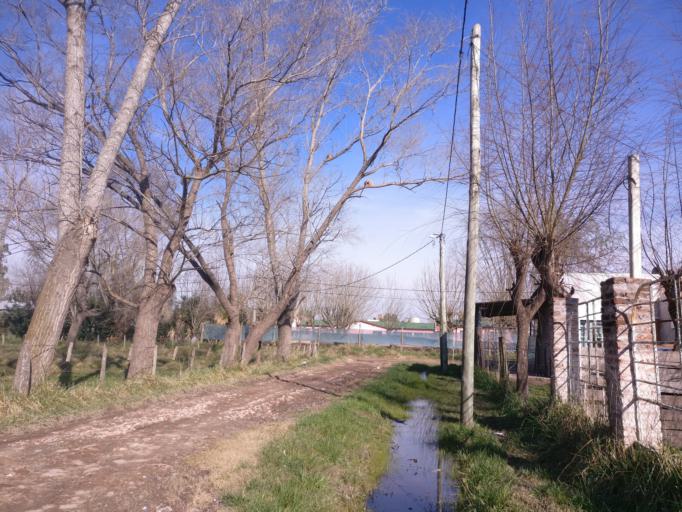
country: AR
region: Buenos Aires
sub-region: Partido de Ezeiza
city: Ezeiza
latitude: -34.9365
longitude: -58.6149
